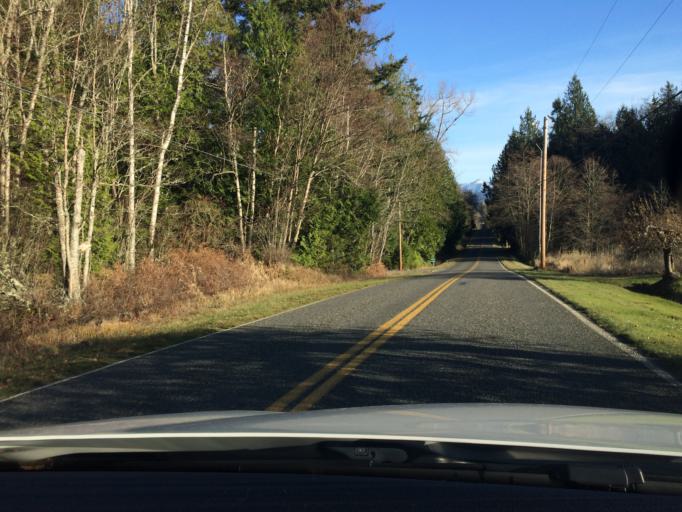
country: US
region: Washington
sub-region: Whatcom County
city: Geneva
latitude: 48.8186
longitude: -122.4065
